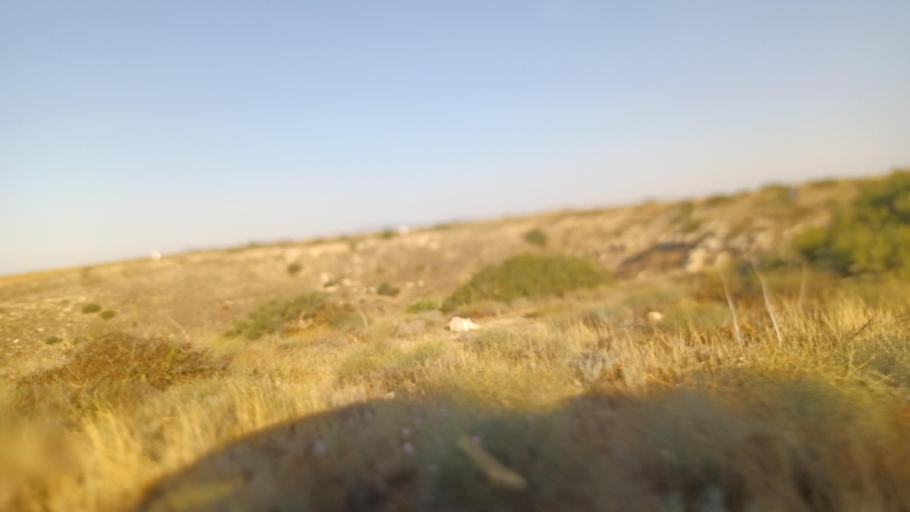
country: CY
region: Larnaka
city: Pyla
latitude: 34.9952
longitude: 33.7058
